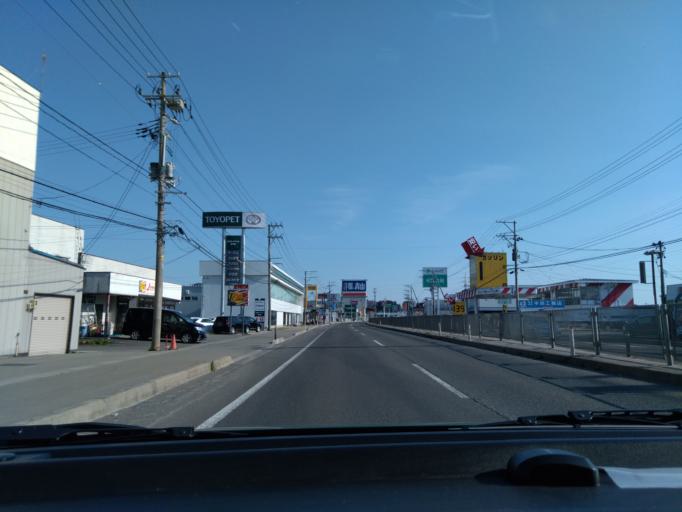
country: JP
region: Akita
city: Yokotemachi
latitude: 39.3087
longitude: 140.5573
